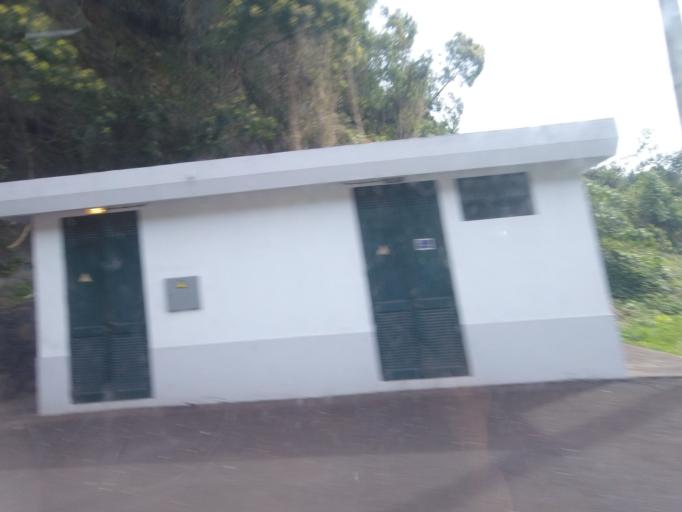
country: PT
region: Madeira
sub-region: Santana
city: Santana
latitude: 32.7646
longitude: -16.8356
